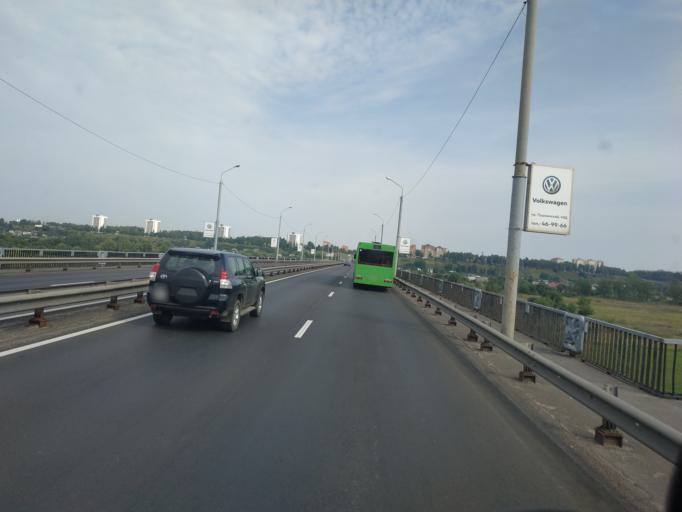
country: BY
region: Mogilev
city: Mahilyow
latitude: 53.8916
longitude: 30.3751
